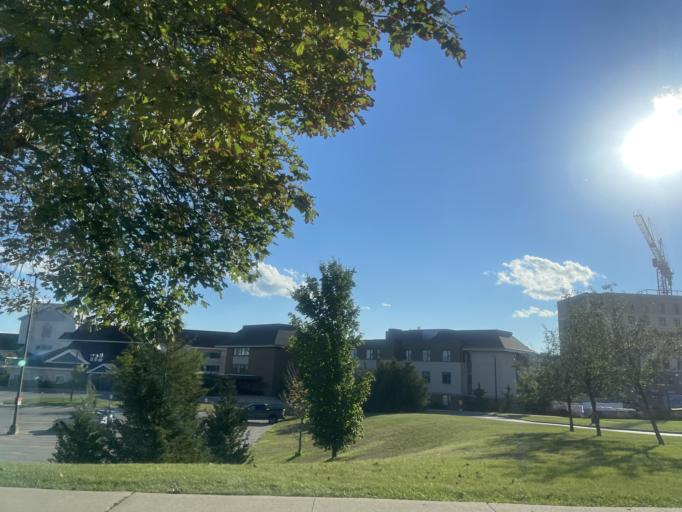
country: CA
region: Ontario
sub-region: Wellington County
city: Guelph
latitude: 43.5514
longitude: -80.2716
